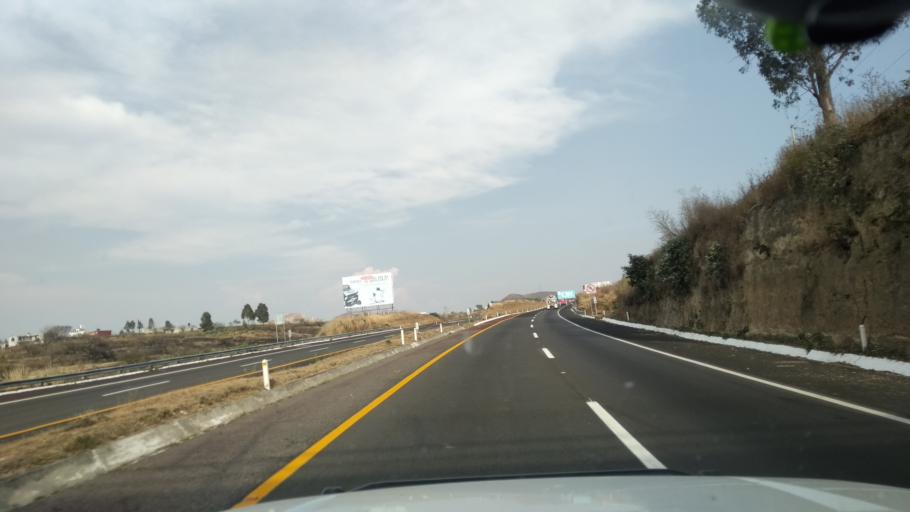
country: MX
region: Puebla
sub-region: Santa Isabel Cholula
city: San Pablo Ahuatempa
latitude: 18.9774
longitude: -98.3576
